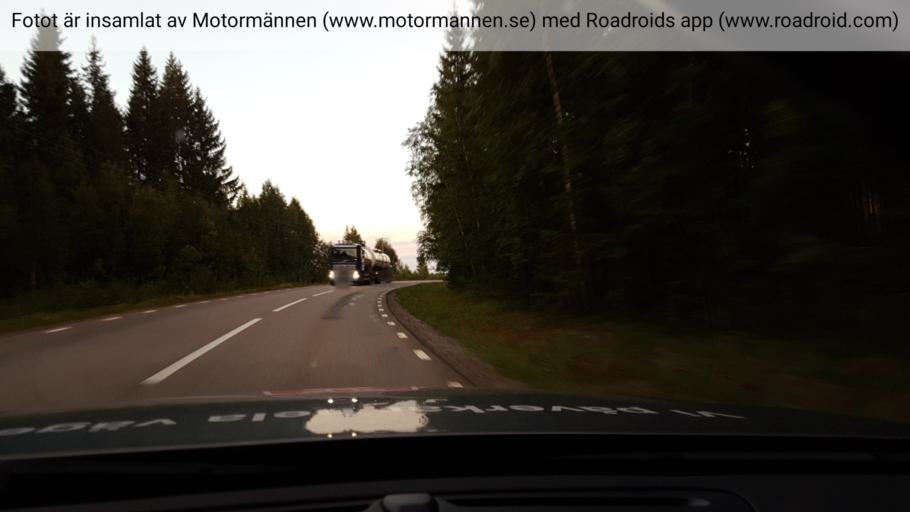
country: SE
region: OErebro
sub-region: Hallefors Kommun
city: Haellefors
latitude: 59.6803
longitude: 14.5040
